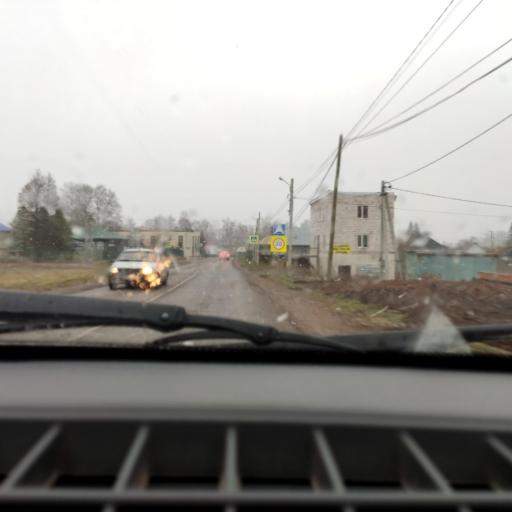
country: RU
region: Bashkortostan
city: Avdon
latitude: 54.6552
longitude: 55.7602
